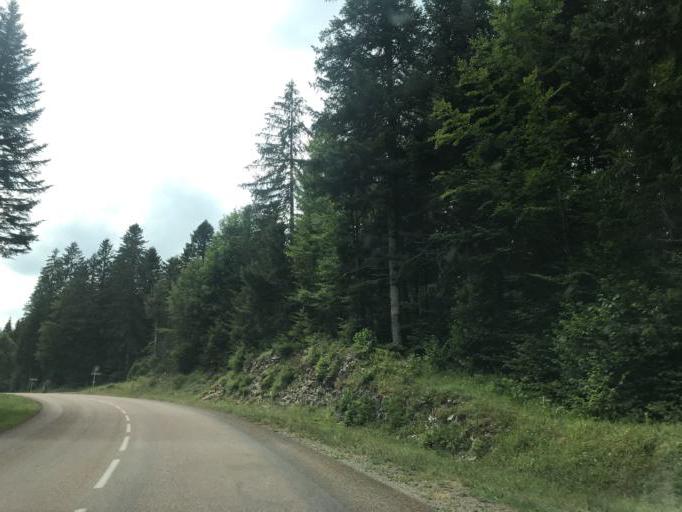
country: FR
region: Franche-Comte
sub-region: Departement du Jura
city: Longchaumois
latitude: 46.5009
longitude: 5.9166
